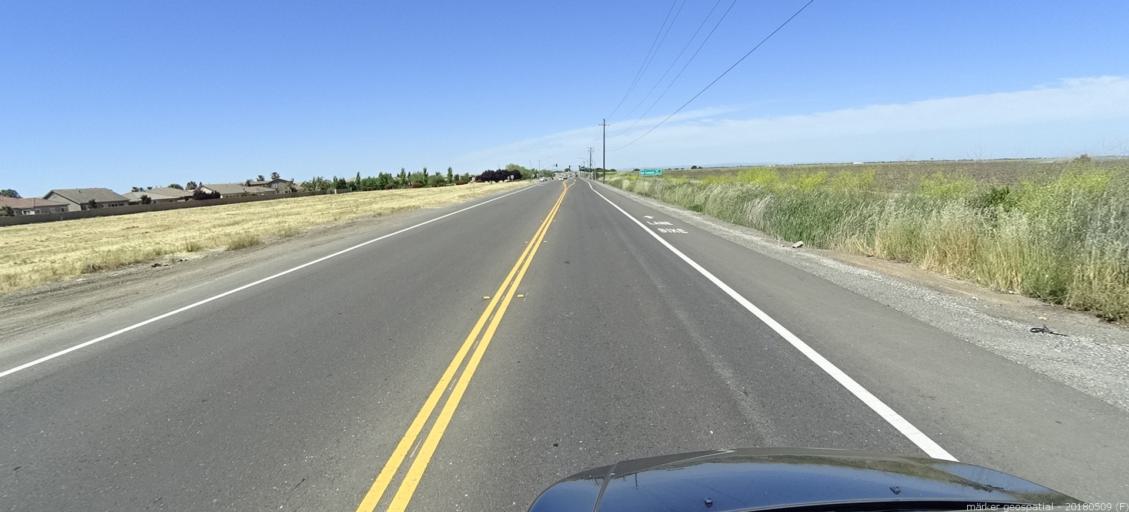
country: US
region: California
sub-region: Sacramento County
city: Elverta
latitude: 38.6856
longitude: -121.5283
